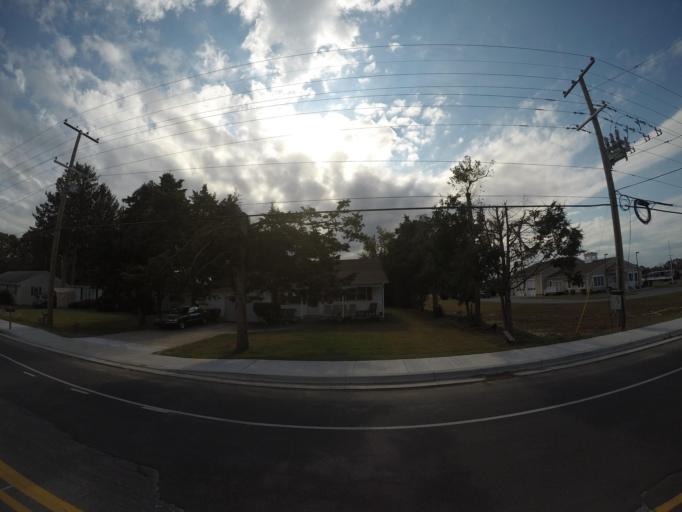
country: US
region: Delaware
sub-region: Sussex County
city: Lewes
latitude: 38.7250
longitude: -75.1438
